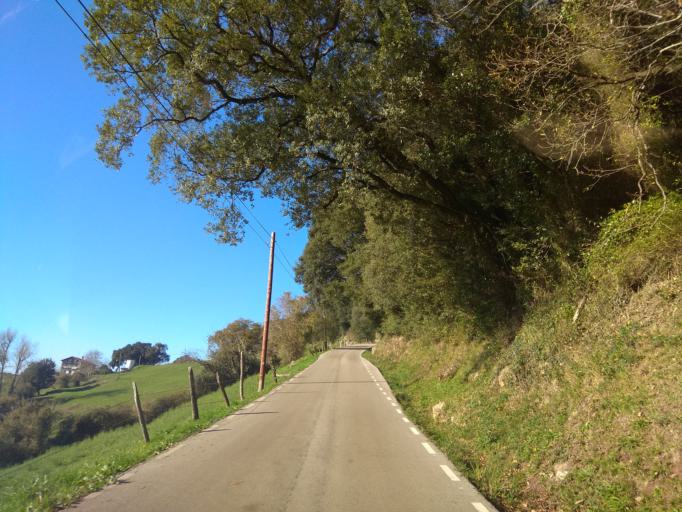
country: ES
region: Cantabria
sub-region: Provincia de Cantabria
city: Entrambasaguas
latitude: 43.3771
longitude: -3.6965
